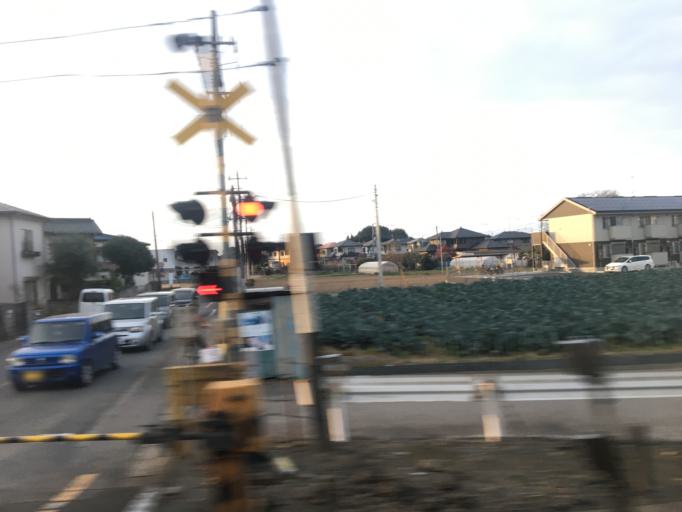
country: JP
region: Ibaraki
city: Koga
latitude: 36.1566
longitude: 139.7135
